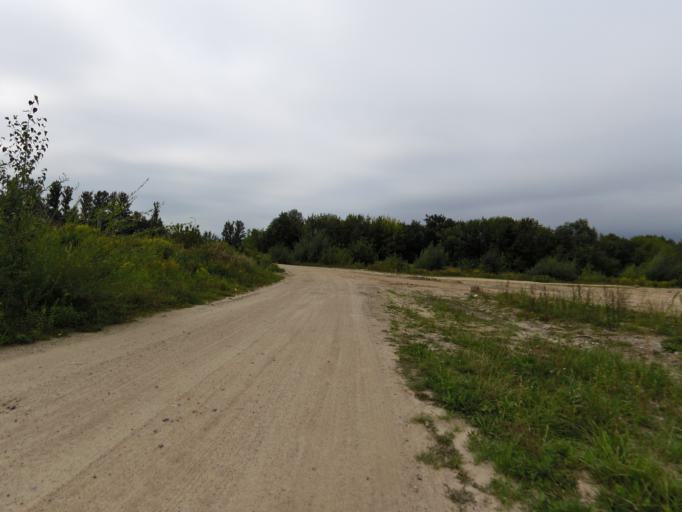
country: LT
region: Vilnius County
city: Rasos
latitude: 54.6575
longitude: 25.2917
